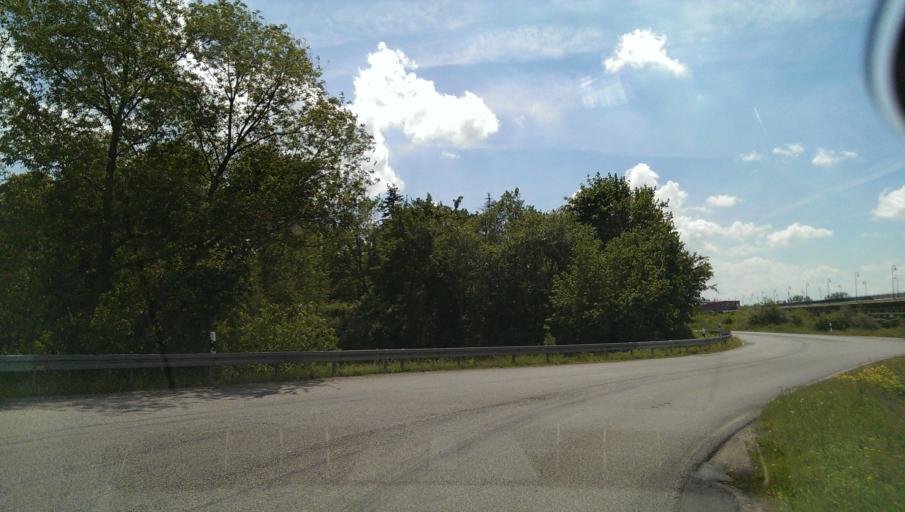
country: DE
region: Saxony-Anhalt
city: Schonebeck
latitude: 52.0285
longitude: 11.7427
